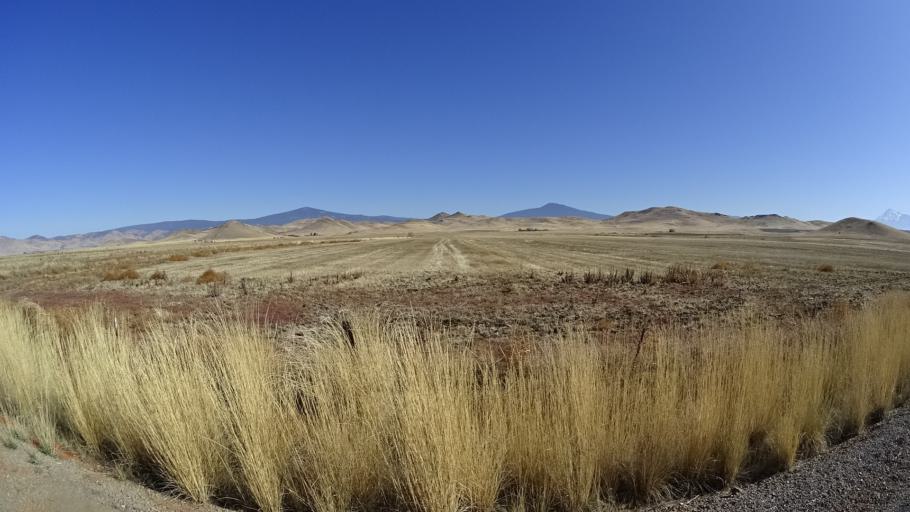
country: US
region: California
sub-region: Siskiyou County
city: Montague
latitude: 41.7627
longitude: -122.4571
